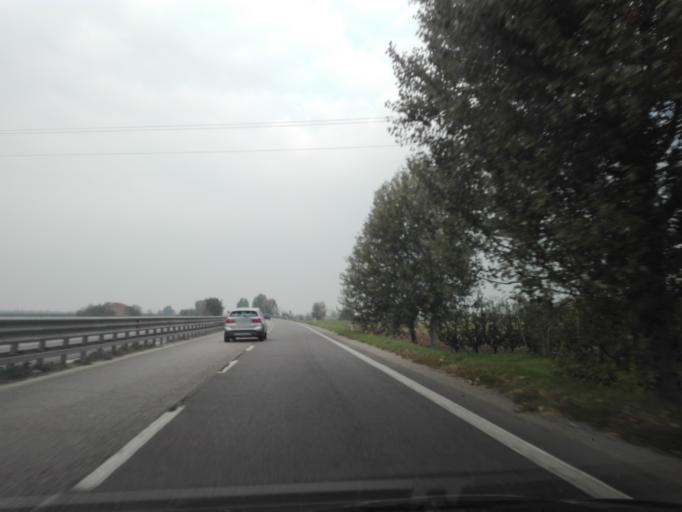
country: IT
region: Veneto
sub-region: Provincia di Verona
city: Villa Bartolomea
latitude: 45.1491
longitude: 11.3428
